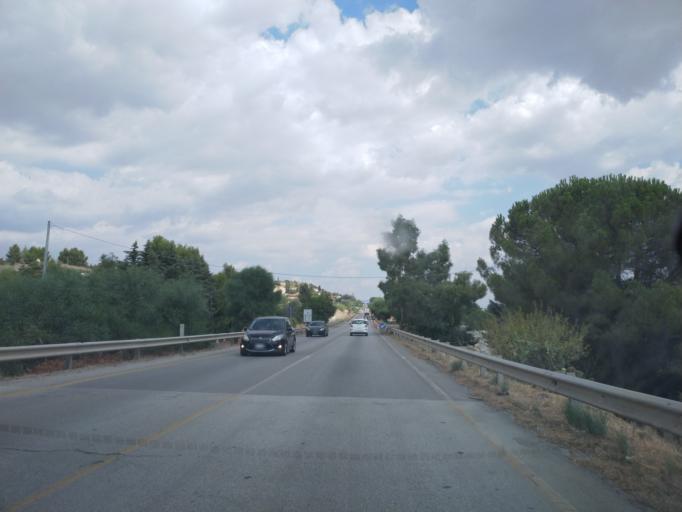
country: IT
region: Sicily
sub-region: Provincia di Caltanissetta
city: San Cataldo
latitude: 37.4743
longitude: 14.0156
